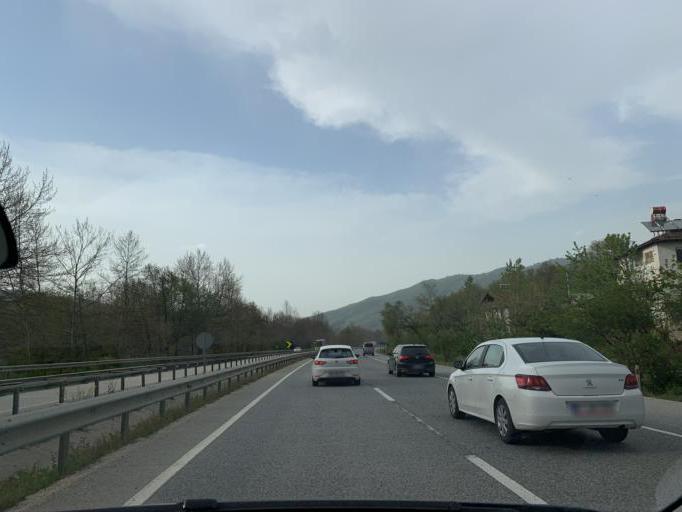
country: TR
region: Bursa
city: Tahtakopru
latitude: 39.9656
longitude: 29.6560
